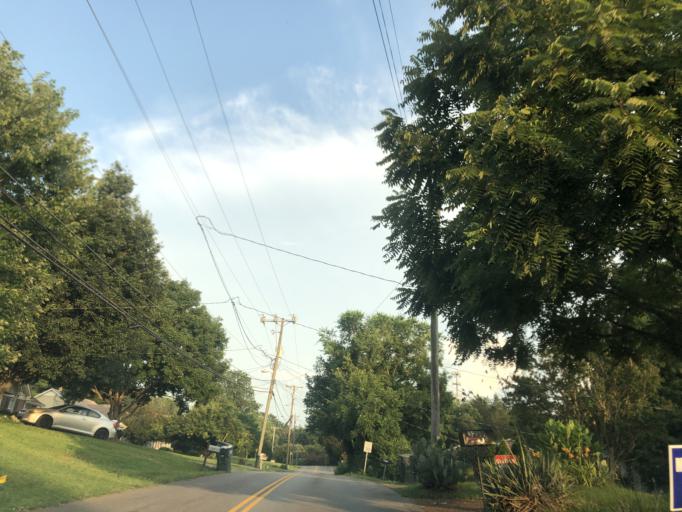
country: US
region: Tennessee
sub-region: Davidson County
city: Lakewood
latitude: 36.1370
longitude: -86.6337
